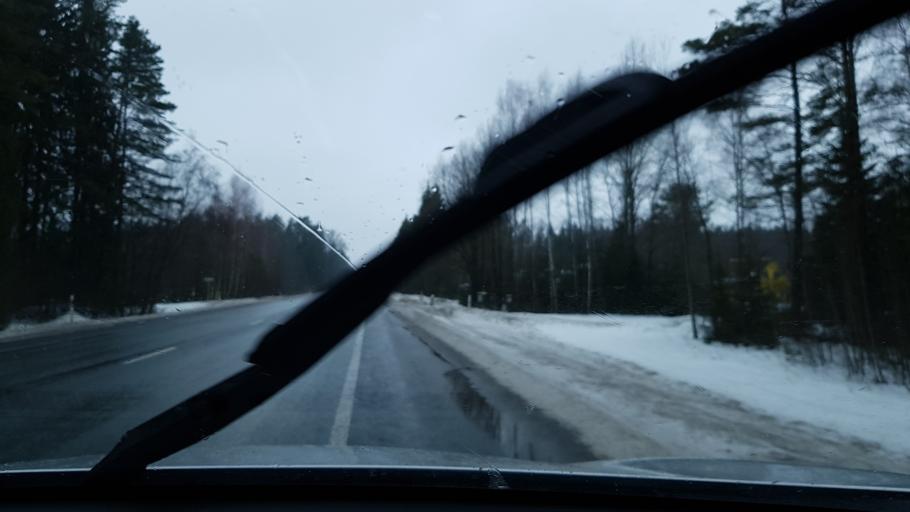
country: EE
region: Raplamaa
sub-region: Kohila vald
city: Kohila
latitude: 59.1483
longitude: 24.7839
